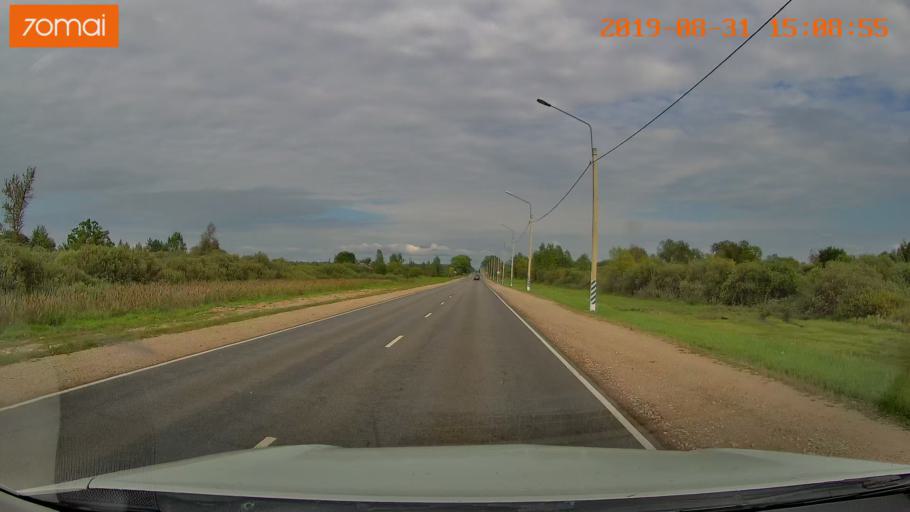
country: RU
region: Kaluga
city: Spas-Demensk
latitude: 54.3964
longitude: 34.1916
